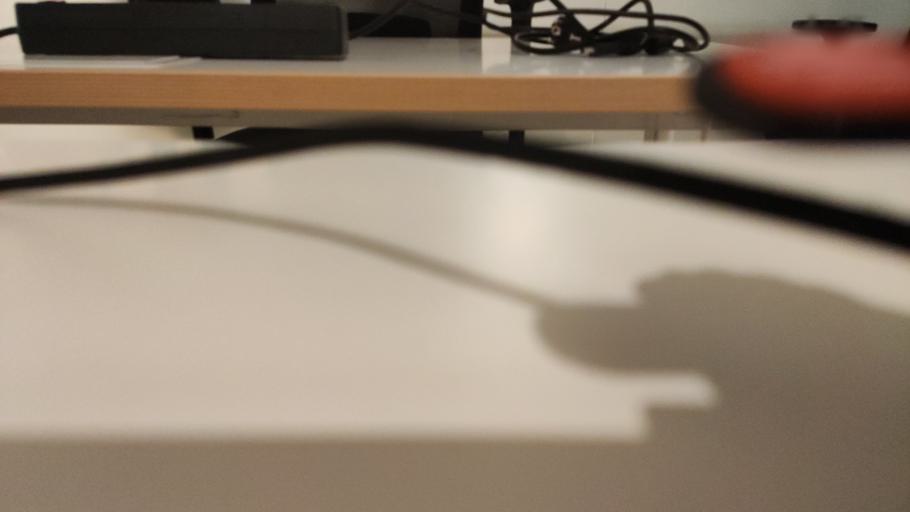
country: RU
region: Moskovskaya
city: Obolensk
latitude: 54.9947
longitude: 37.2668
